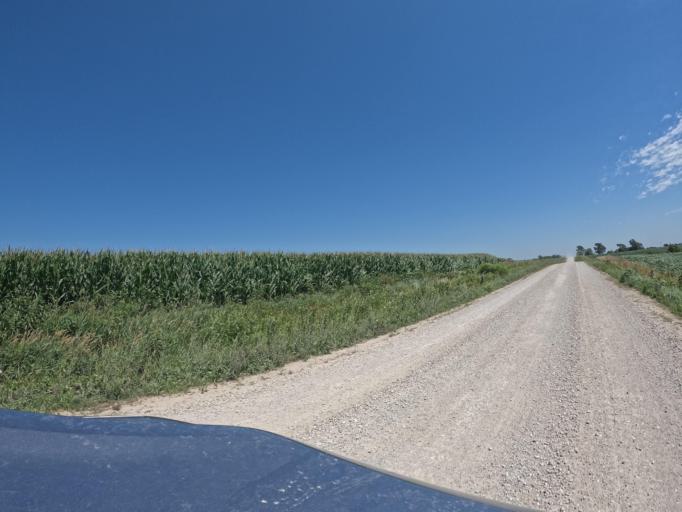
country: US
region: Iowa
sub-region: Keokuk County
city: Sigourney
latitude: 41.4522
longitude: -92.3613
